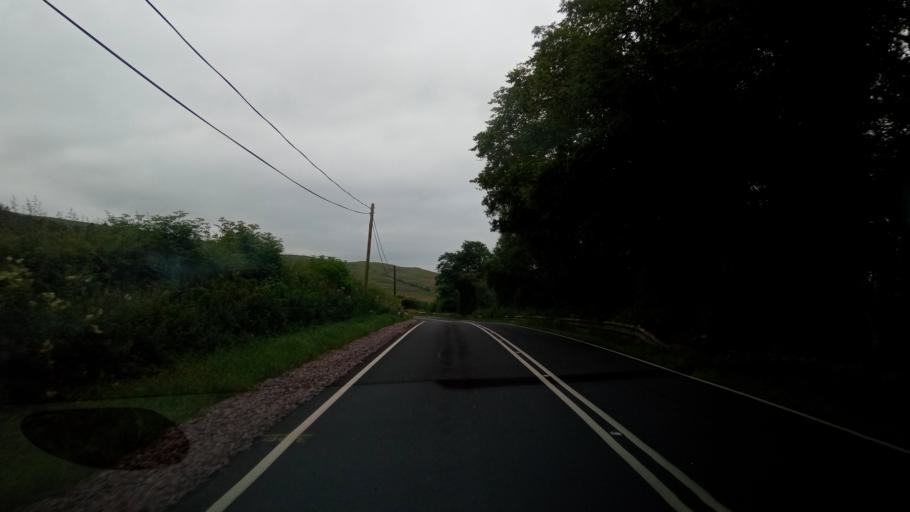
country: GB
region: Scotland
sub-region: The Scottish Borders
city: Hawick
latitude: 55.3500
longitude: -2.9189
